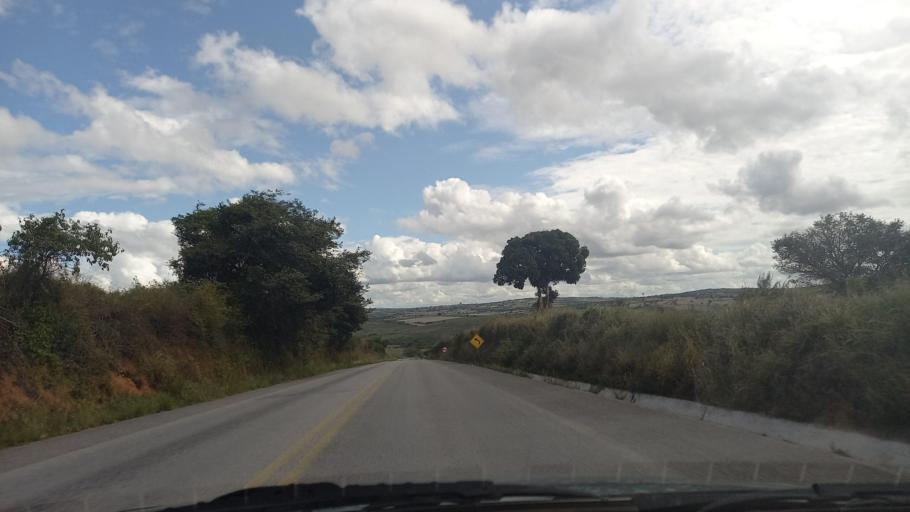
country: BR
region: Pernambuco
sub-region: Lajedo
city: Lajedo
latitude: -8.7241
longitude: -36.4287
